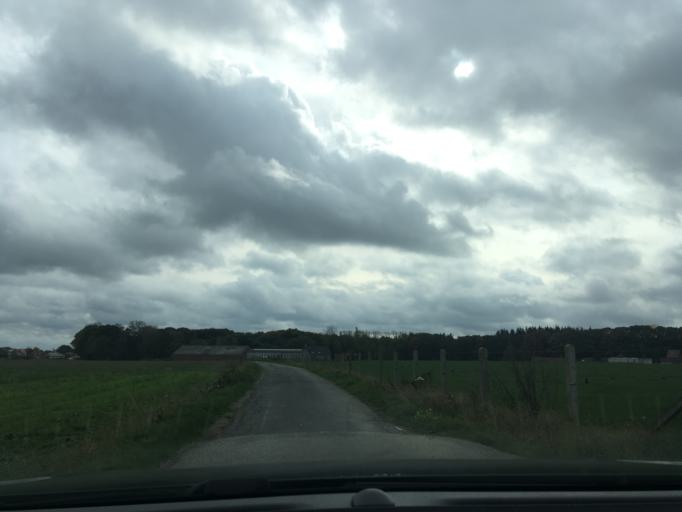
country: BE
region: Flanders
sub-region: Provincie West-Vlaanderen
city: Zonnebeke
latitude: 50.8451
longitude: 2.9702
